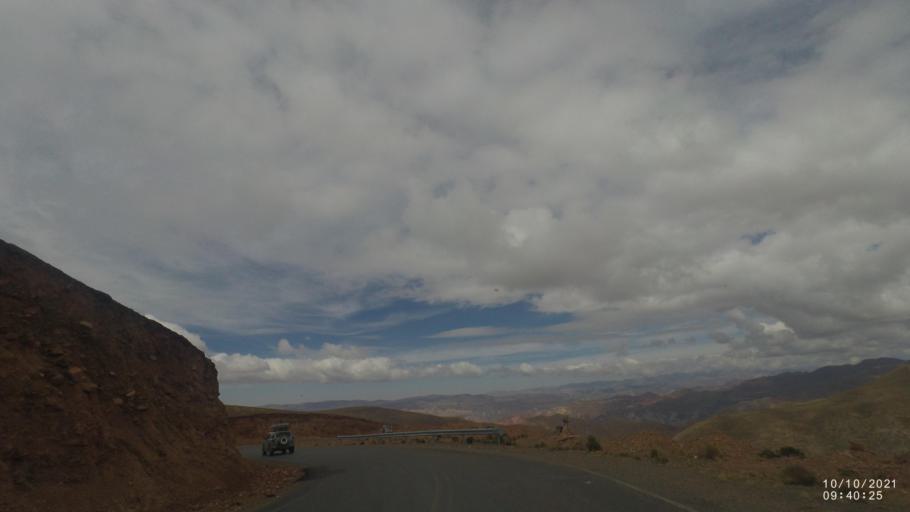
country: BO
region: La Paz
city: Quime
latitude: -17.1391
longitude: -67.3414
